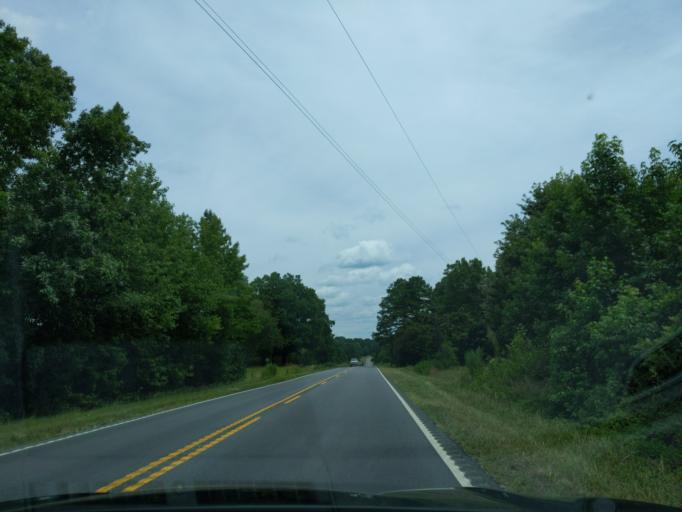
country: US
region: North Carolina
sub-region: Cabarrus County
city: Mount Pleasant
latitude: 35.4496
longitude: -80.3512
